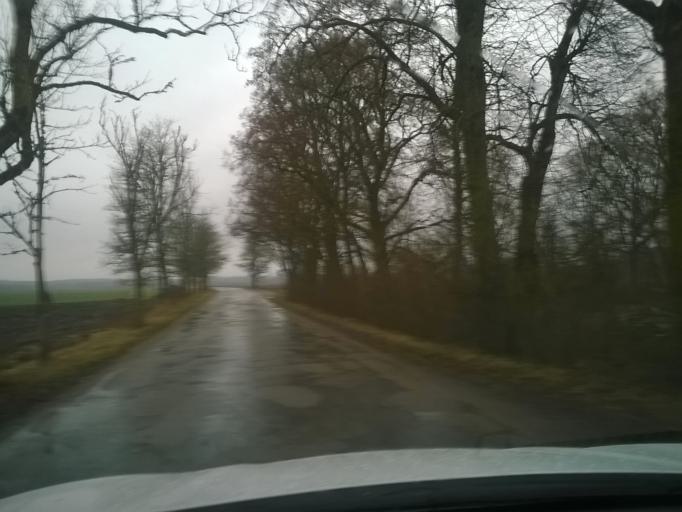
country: LV
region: Jaunpils
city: Jaunpils
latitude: 56.8488
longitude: 23.0442
